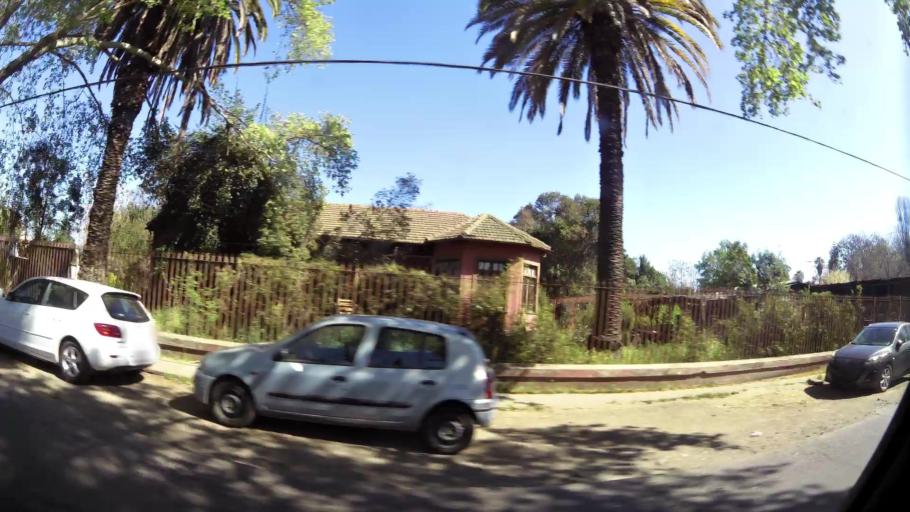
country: CL
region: Santiago Metropolitan
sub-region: Provincia de Talagante
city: Penaflor
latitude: -33.6003
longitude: -70.8926
